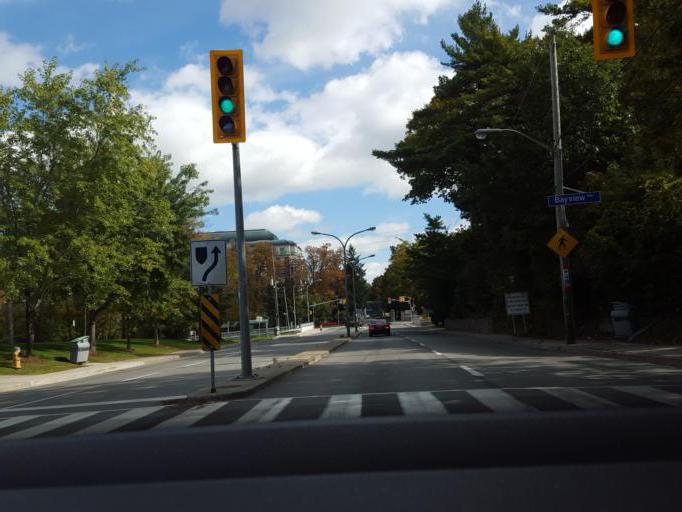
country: CA
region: Ontario
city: Willowdale
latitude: 43.7278
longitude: -79.3837
